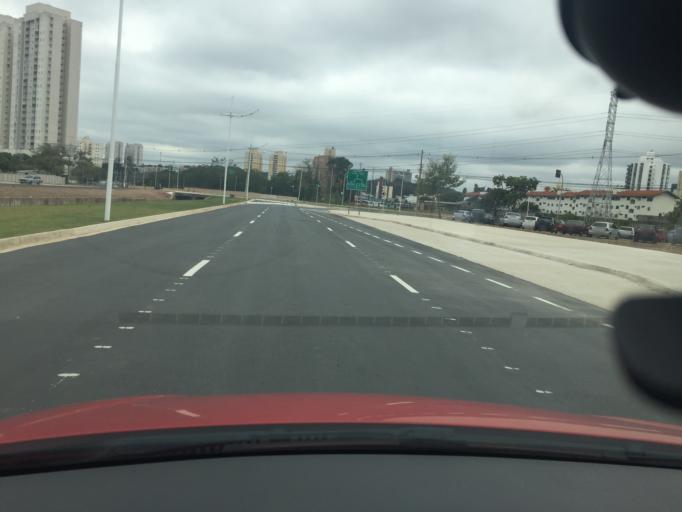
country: BR
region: Sao Paulo
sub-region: Jundiai
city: Jundiai
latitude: -23.1841
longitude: -46.9054
